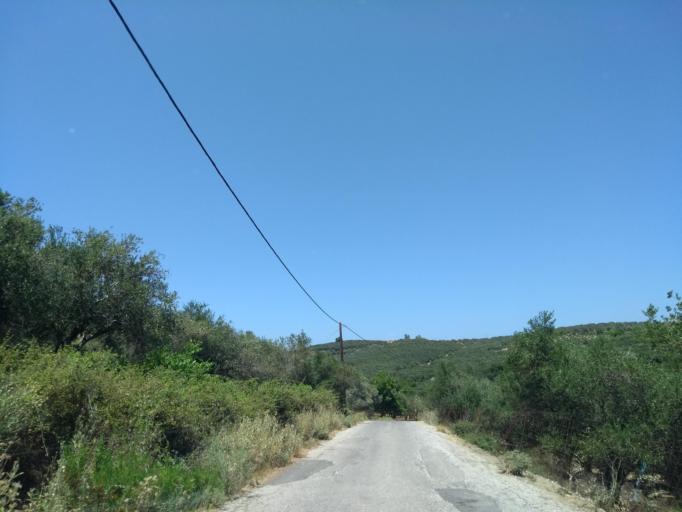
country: GR
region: Crete
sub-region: Nomos Chanias
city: Georgioupolis
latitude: 35.3295
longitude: 24.3208
